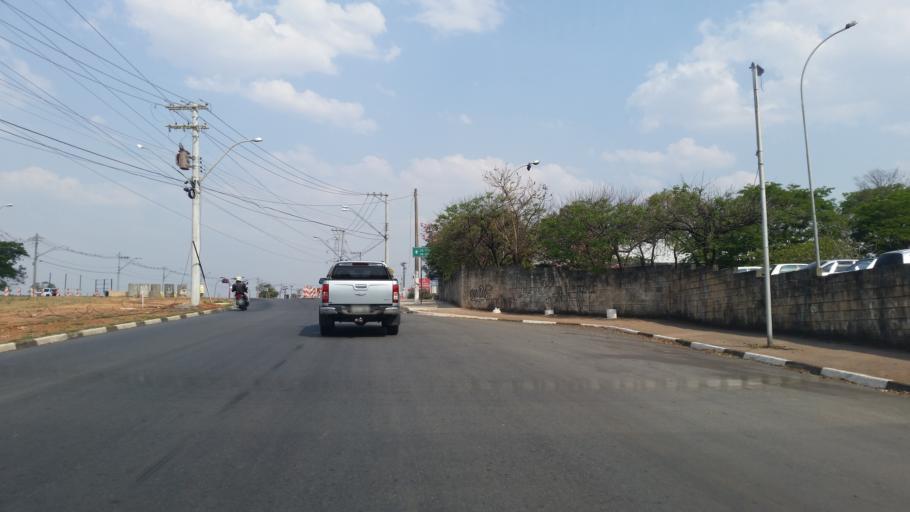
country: BR
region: Sao Paulo
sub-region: Hortolandia
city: Hortolandia
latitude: -22.8849
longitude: -47.1948
